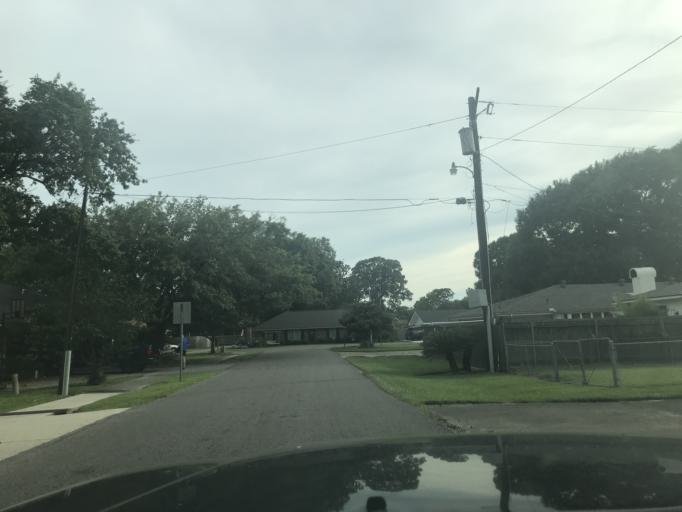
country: US
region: Louisiana
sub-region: Lafayette Parish
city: Lafayette
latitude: 30.1925
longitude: -92.0482
